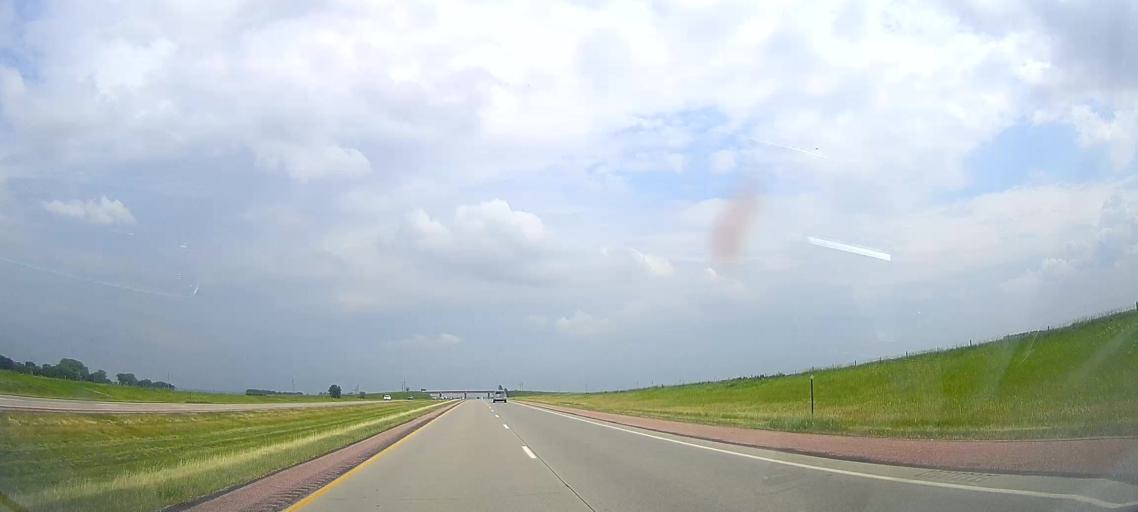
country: US
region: South Dakota
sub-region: Union County
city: Elk Point
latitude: 42.6603
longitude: -96.6507
